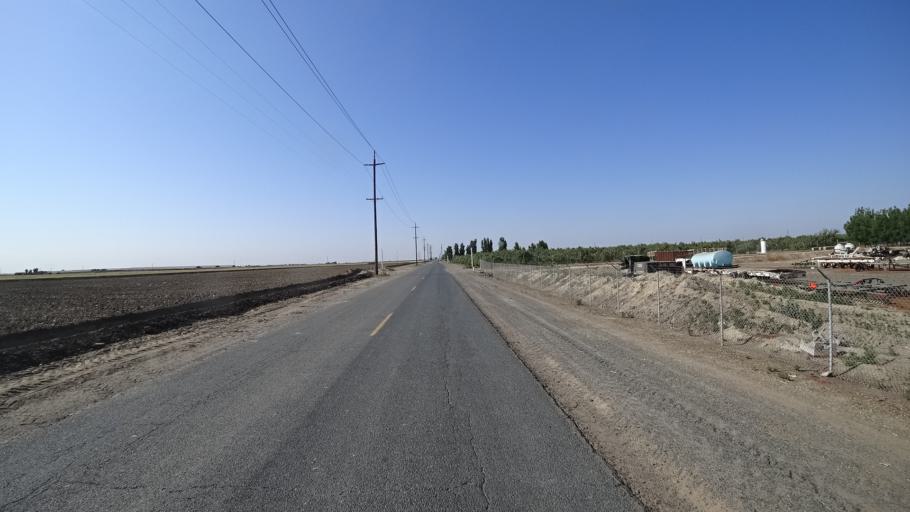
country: US
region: California
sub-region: Kings County
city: Home Garden
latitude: 36.2592
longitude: -119.5831
